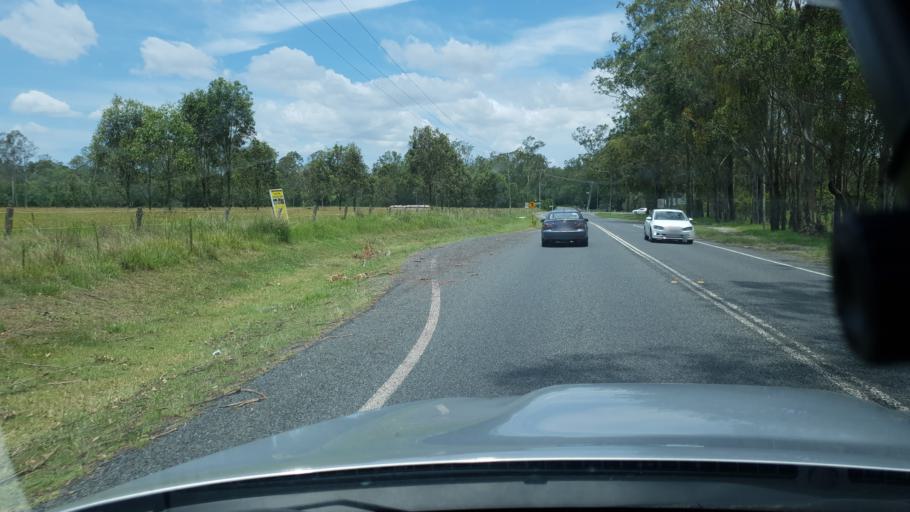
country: AU
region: Queensland
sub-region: Logan
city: North Maclean
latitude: -27.8271
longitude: 153.0131
